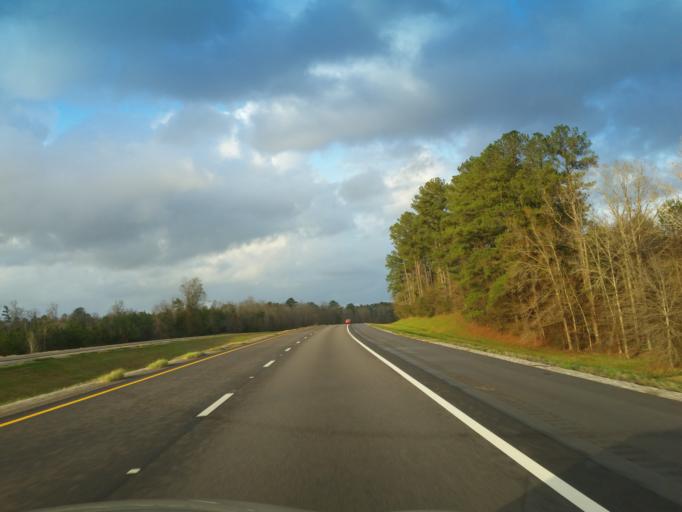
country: US
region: Mississippi
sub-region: Jones County
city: Sharon
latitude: 31.9227
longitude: -89.0034
